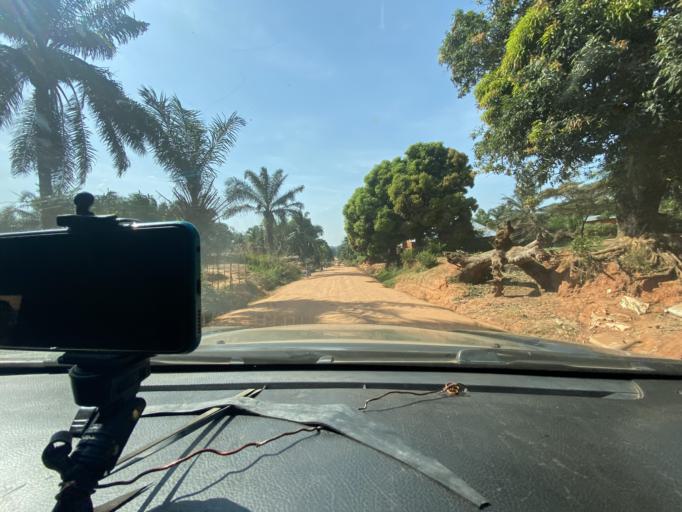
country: CD
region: Kasai-Oriental
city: Kabinda
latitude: -6.1289
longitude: 24.5033
